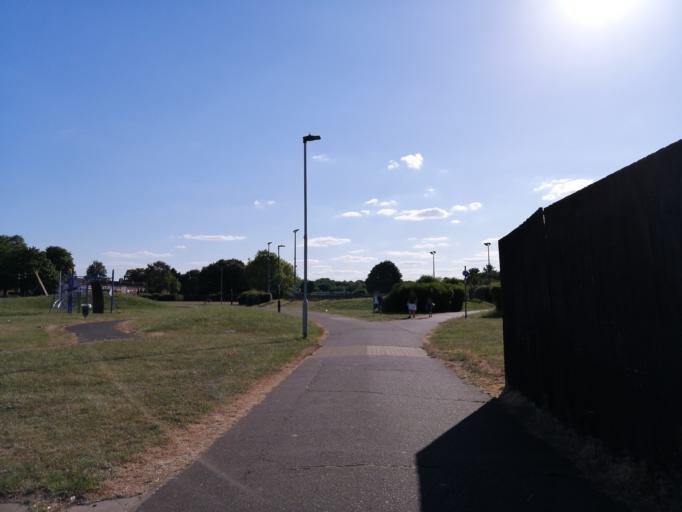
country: GB
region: England
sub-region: Peterborough
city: Peterborough
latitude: 52.5901
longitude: -0.2702
